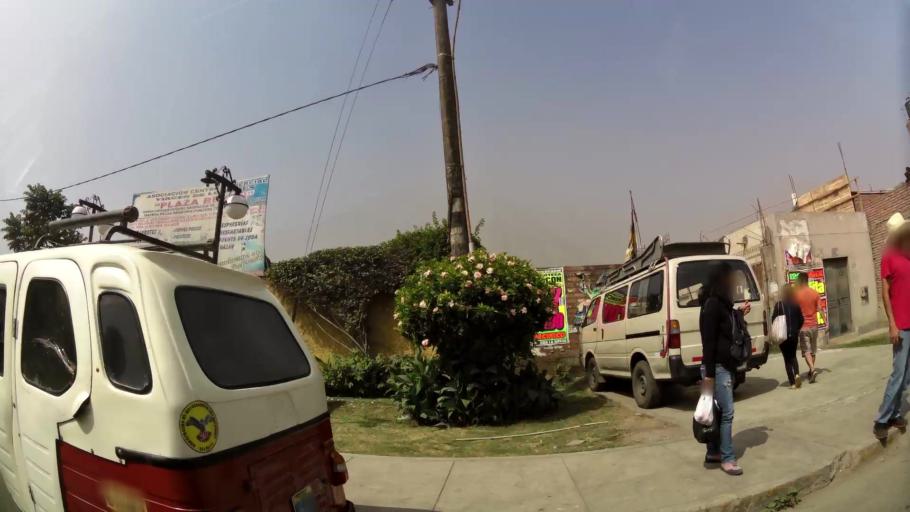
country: PE
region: Lima
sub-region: Lima
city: Asentamiento Humano Nicolas de Pierola
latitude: -11.9395
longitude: -76.6997
